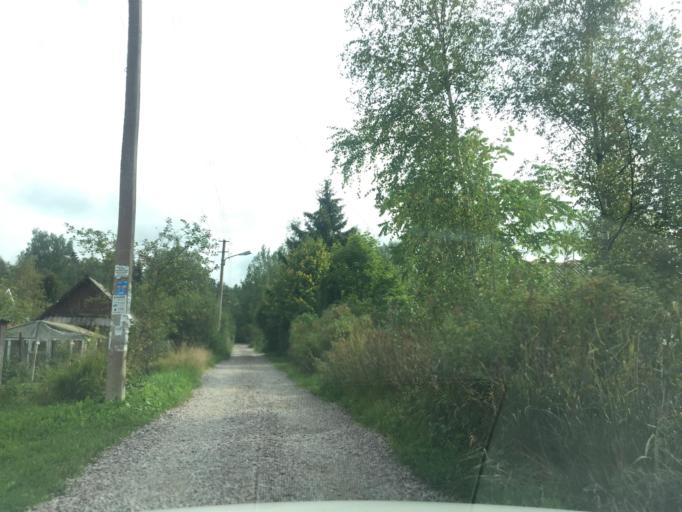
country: RU
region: Leningrad
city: Siverskiy
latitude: 59.2962
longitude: 30.0304
